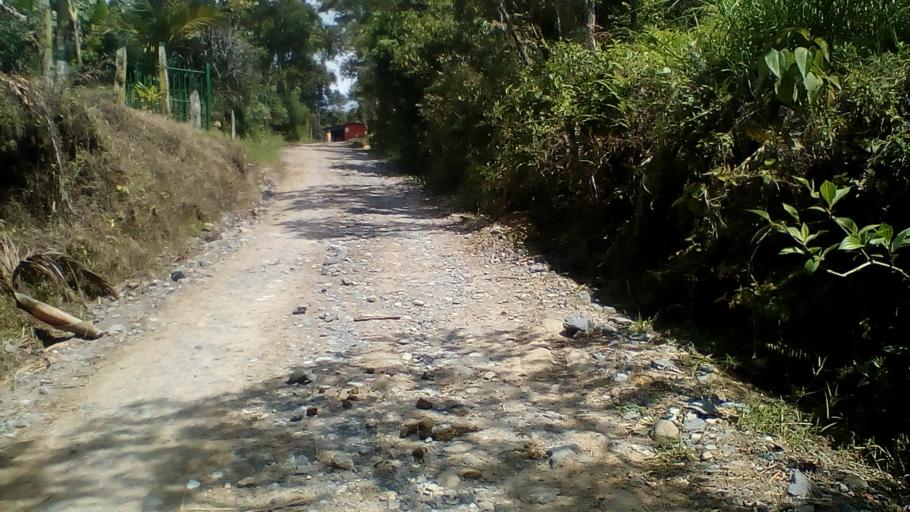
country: CO
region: Boyaca
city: Santana
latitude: 6.0005
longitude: -73.5066
